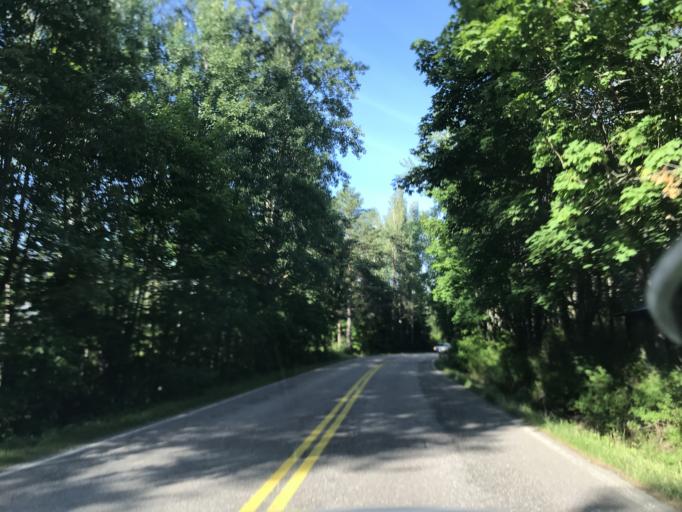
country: FI
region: Uusimaa
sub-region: Helsinki
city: Vihti
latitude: 60.4354
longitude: 24.5400
